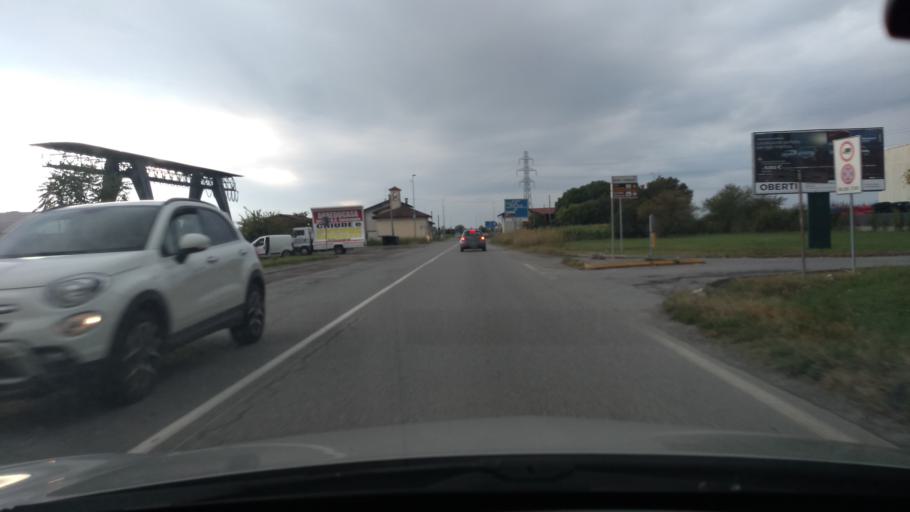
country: IT
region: Lombardy
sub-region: Provincia di Bergamo
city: Pognano
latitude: 45.5924
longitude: 9.6405
